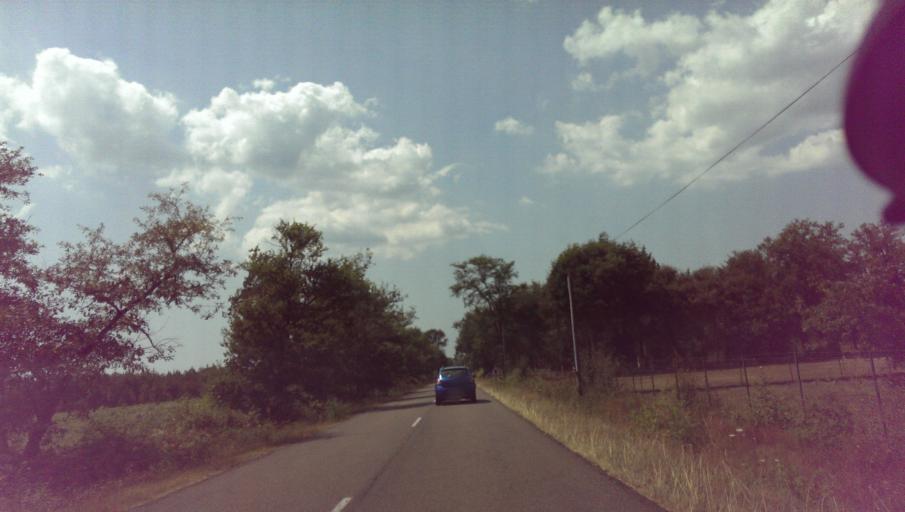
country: FR
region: Aquitaine
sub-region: Departement des Landes
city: Sabres
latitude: 44.1214
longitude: -0.6573
